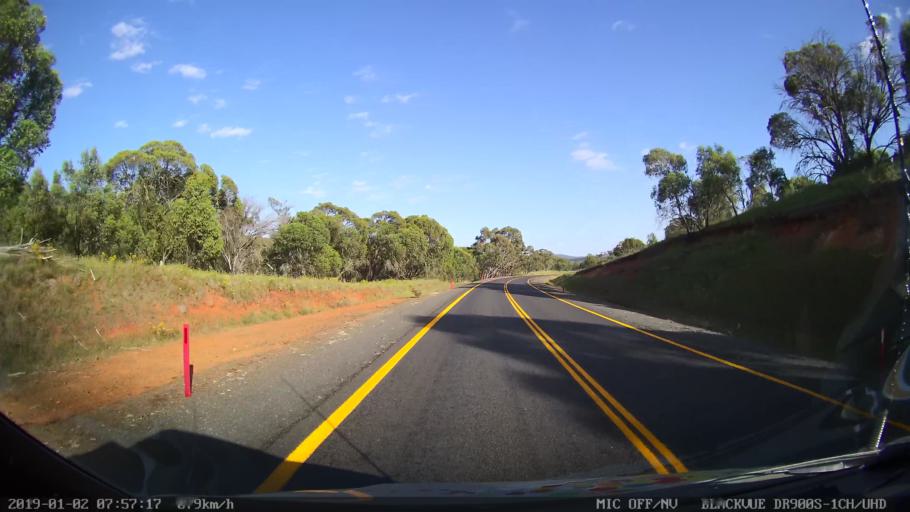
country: AU
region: New South Wales
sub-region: Tumut Shire
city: Tumut
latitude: -35.6653
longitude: 148.4750
